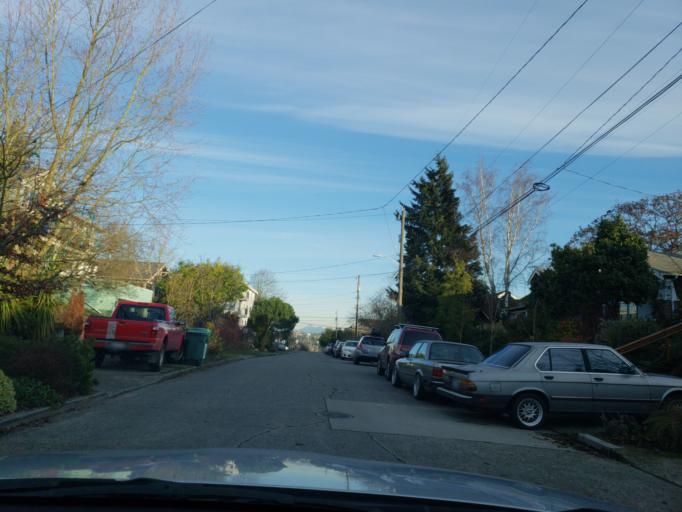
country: US
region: Washington
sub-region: King County
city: Shoreline
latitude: 47.6848
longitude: -122.3570
